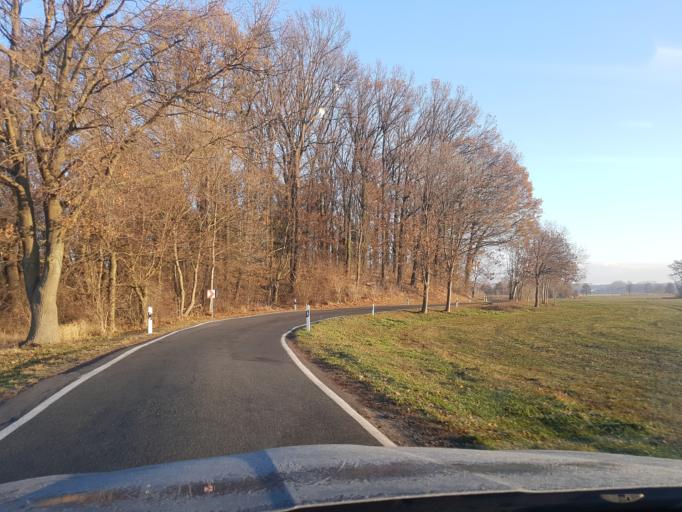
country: DE
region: Brandenburg
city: Schlieben
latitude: 51.7060
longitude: 13.3469
